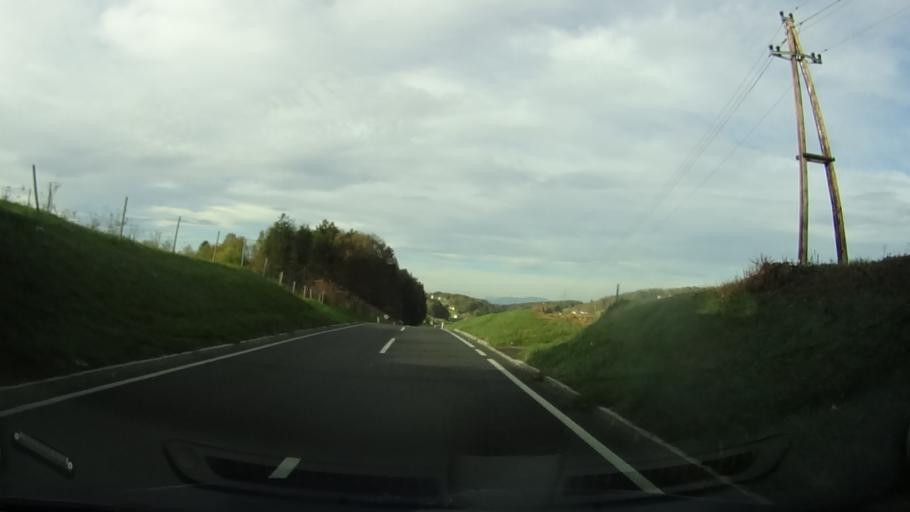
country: AT
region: Styria
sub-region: Politischer Bezirk Deutschlandsberg
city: Preding
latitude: 46.8659
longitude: 15.4086
